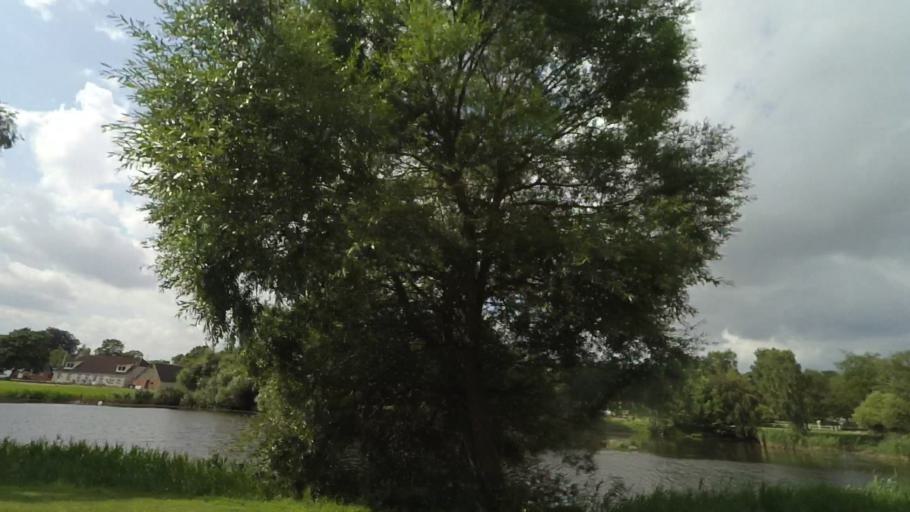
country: DK
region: Central Jutland
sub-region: Norddjurs Kommune
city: Allingabro
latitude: 56.5393
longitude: 10.3647
